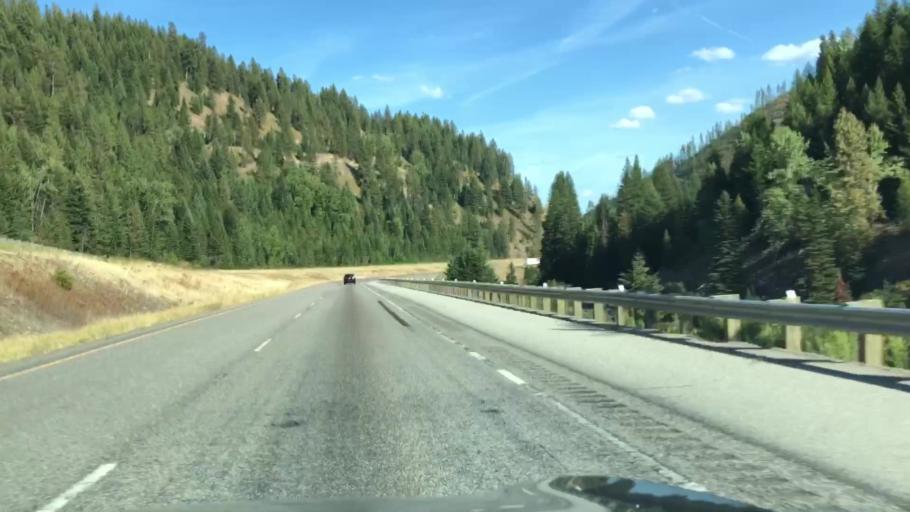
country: US
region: Montana
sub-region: Sanders County
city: Thompson Falls
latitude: 47.4042
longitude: -115.4802
